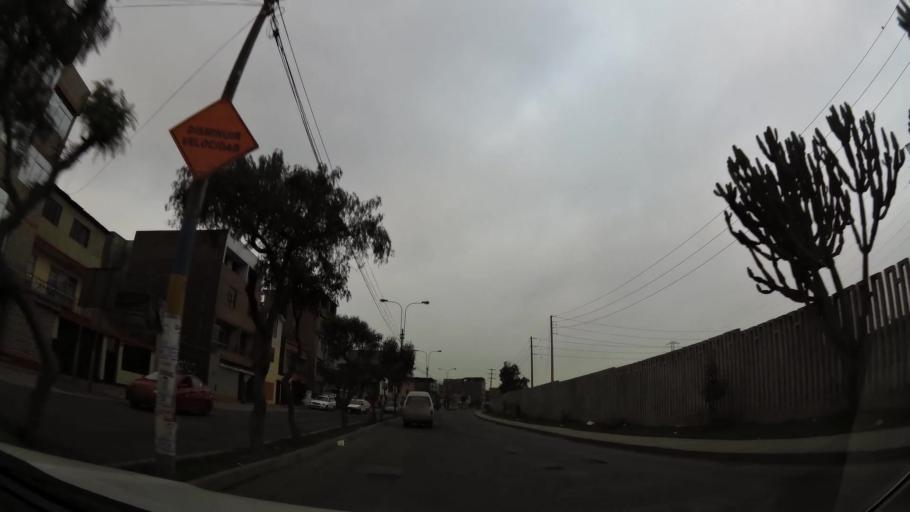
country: PE
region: Lima
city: Lima
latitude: -12.0303
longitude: -77.0098
